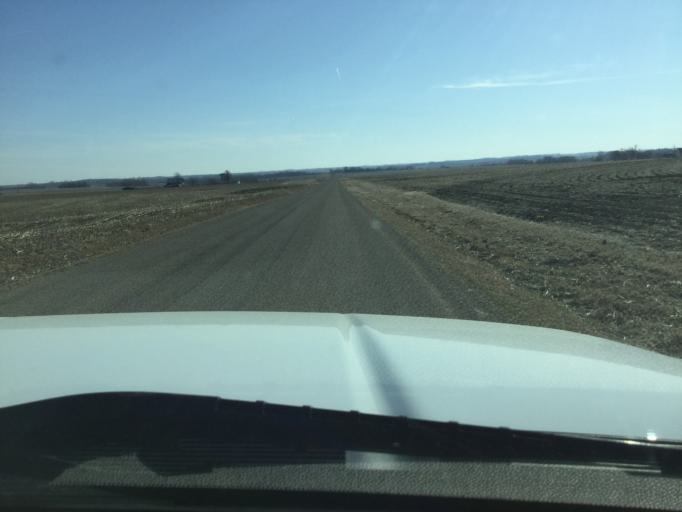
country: US
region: Kansas
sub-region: Brown County
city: Horton
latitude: 39.7255
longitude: -95.4417
